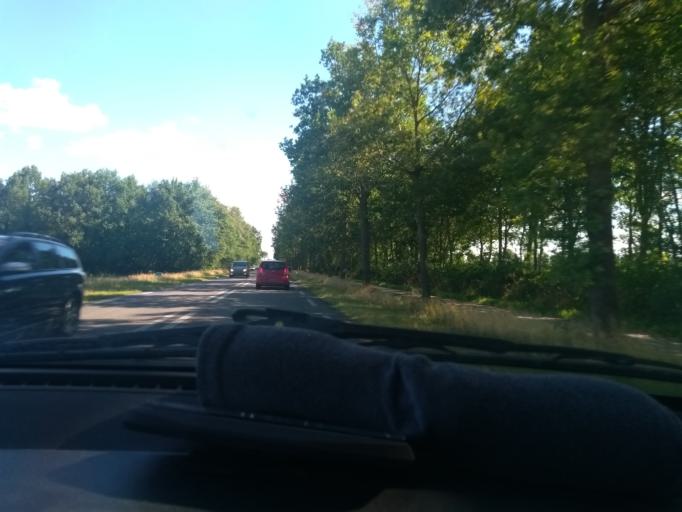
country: NL
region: Drenthe
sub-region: Gemeente Tynaarlo
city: Vries
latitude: 53.1326
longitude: 6.4994
